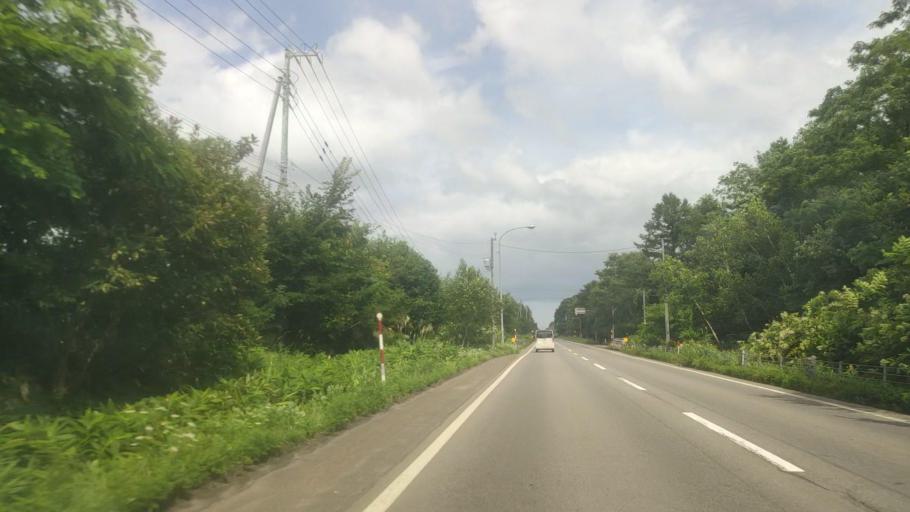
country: JP
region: Hokkaido
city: Nanae
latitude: 42.0285
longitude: 140.6110
